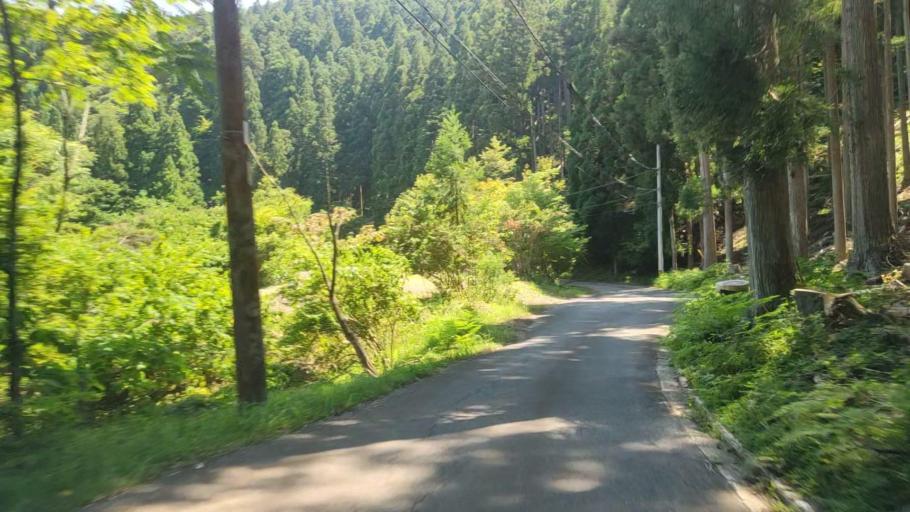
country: JP
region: Gifu
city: Godo
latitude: 35.6905
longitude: 136.5657
